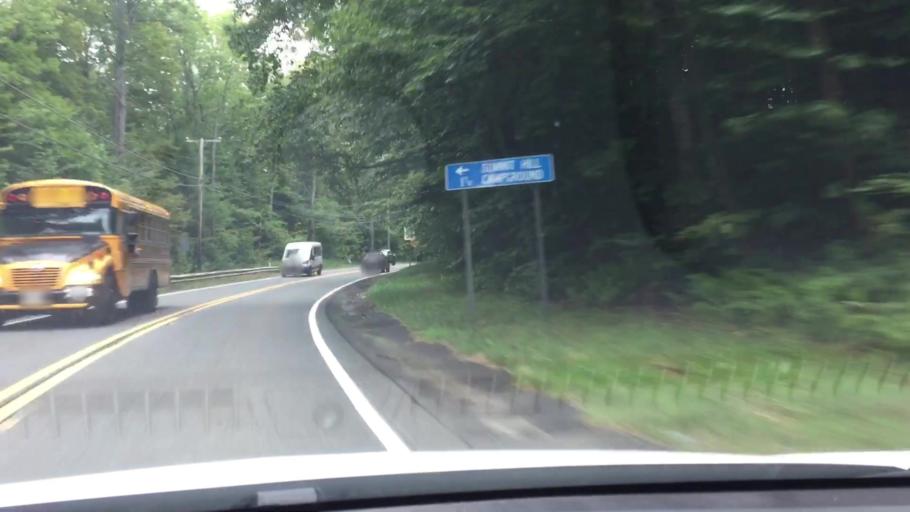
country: US
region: Massachusetts
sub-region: Berkshire County
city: Becket
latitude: 42.3758
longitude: -73.1174
